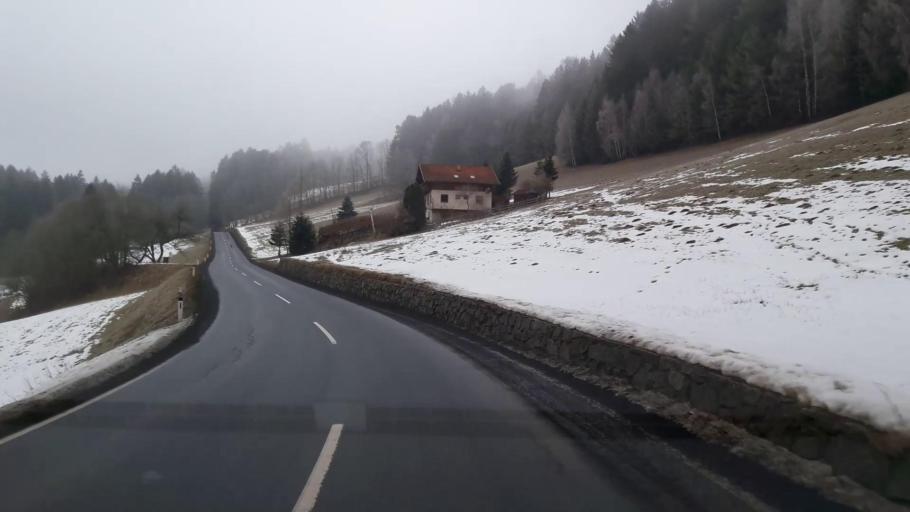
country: AT
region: Lower Austria
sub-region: Politischer Bezirk Neunkirchen
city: Feistritz am Wechsel
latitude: 47.5691
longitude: 16.0426
